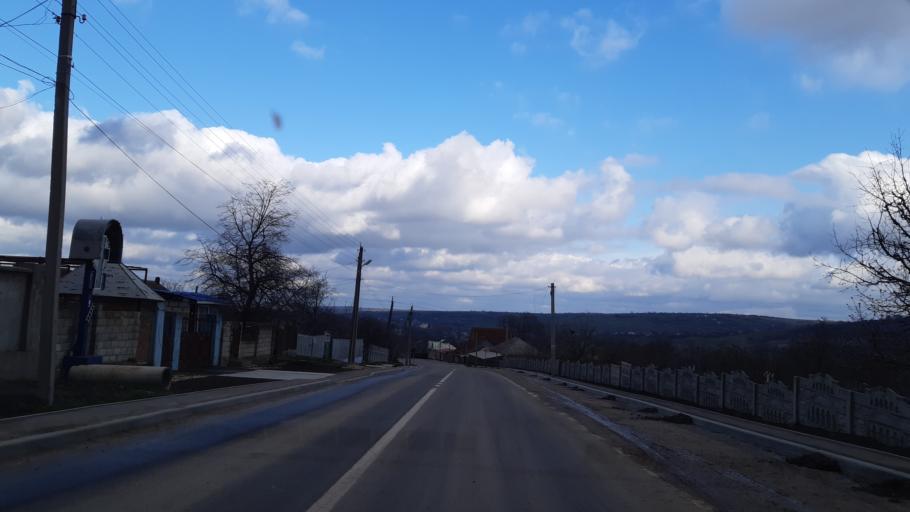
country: MD
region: Telenesti
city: Cocieri
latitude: 47.2235
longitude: 29.0000
